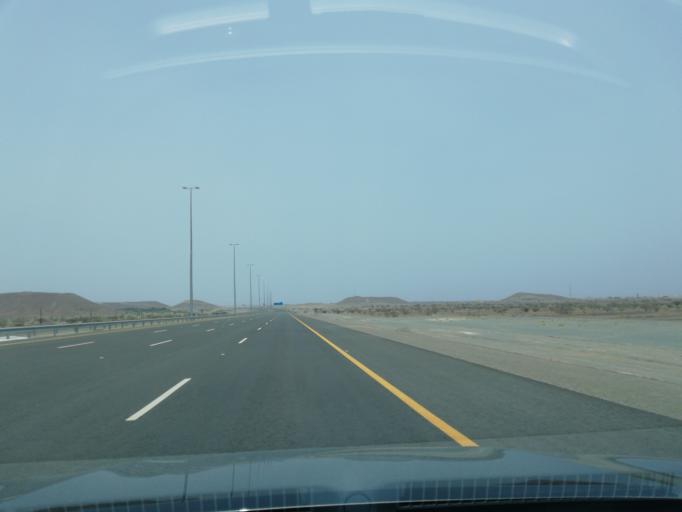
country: OM
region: Al Batinah
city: Al Liwa'
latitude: 24.5073
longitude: 56.5058
